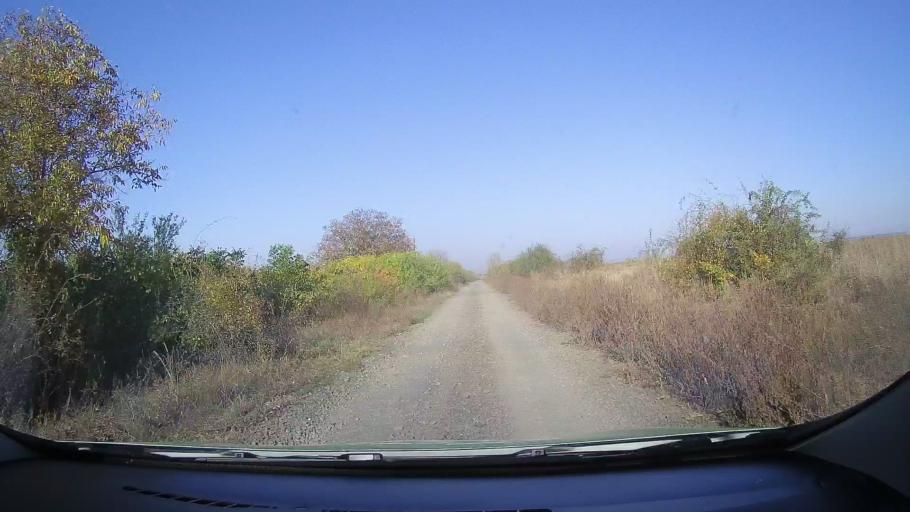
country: RO
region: Satu Mare
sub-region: Comuna Sauca
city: Sauca
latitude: 47.4743
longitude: 22.4805
